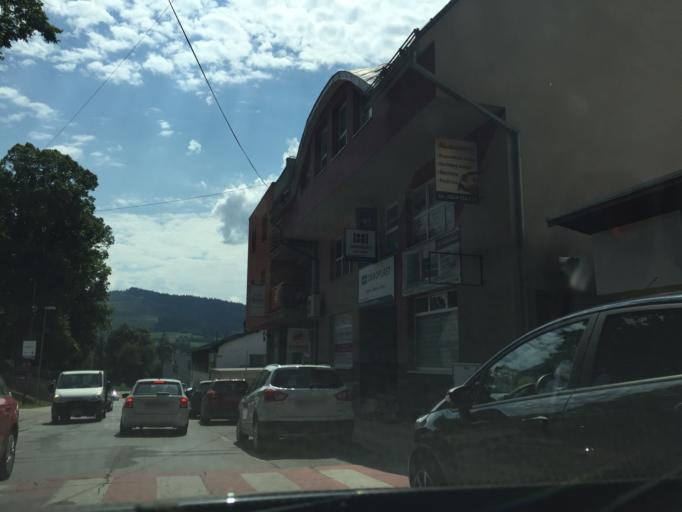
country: SK
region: Zilinsky
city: Namestovo
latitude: 49.4054
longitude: 19.4803
